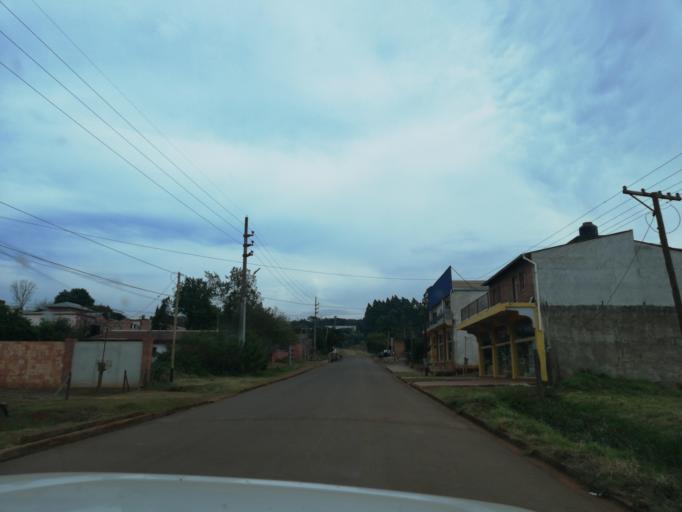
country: AR
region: Misiones
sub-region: Departamento de San Pedro
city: San Pedro
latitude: -26.6263
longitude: -54.1115
